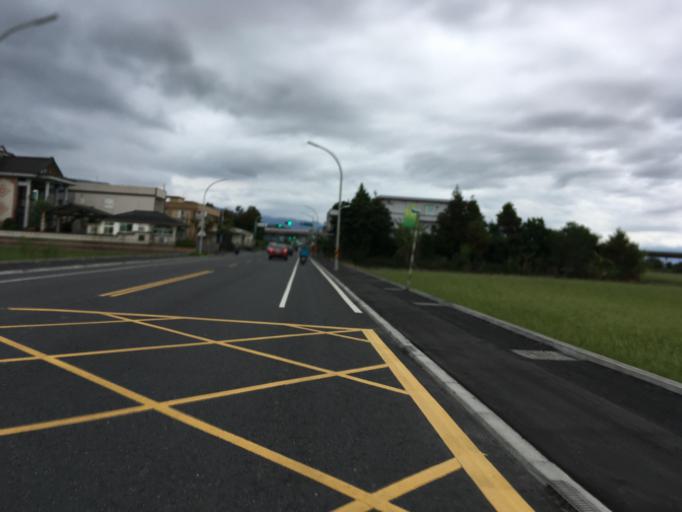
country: TW
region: Taiwan
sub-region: Yilan
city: Yilan
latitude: 24.6423
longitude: 121.8086
